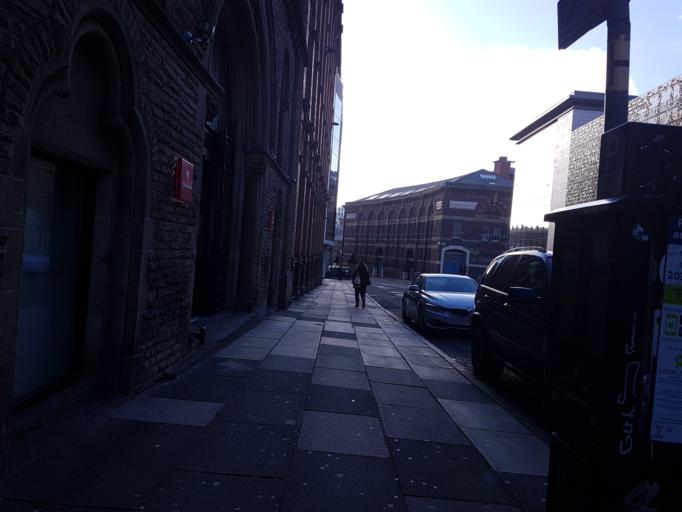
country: GB
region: England
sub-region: Liverpool
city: Liverpool
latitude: 53.4086
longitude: -2.9854
